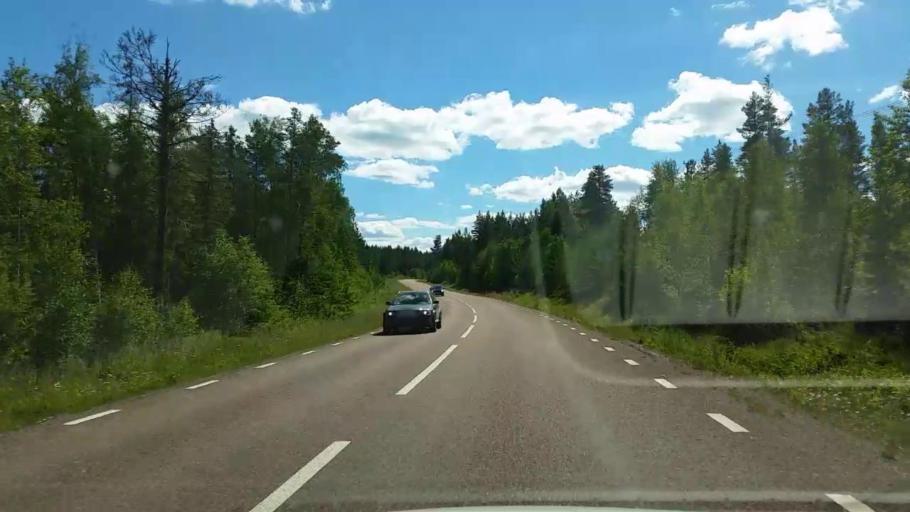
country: SE
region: Dalarna
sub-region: Faluns Kommun
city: Svardsjo
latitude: 60.9775
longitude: 15.6964
